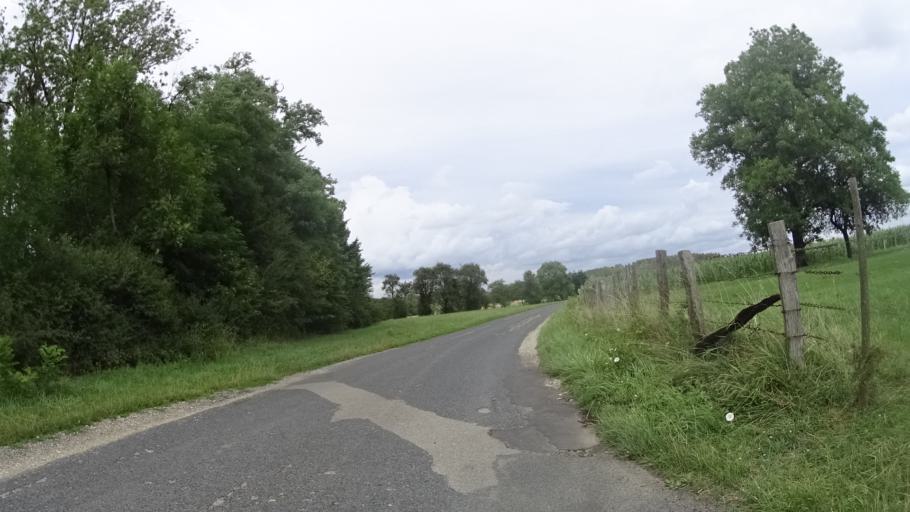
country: FR
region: Lorraine
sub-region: Departement de la Moselle
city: Sarrebourg
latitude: 48.6960
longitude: 7.0548
